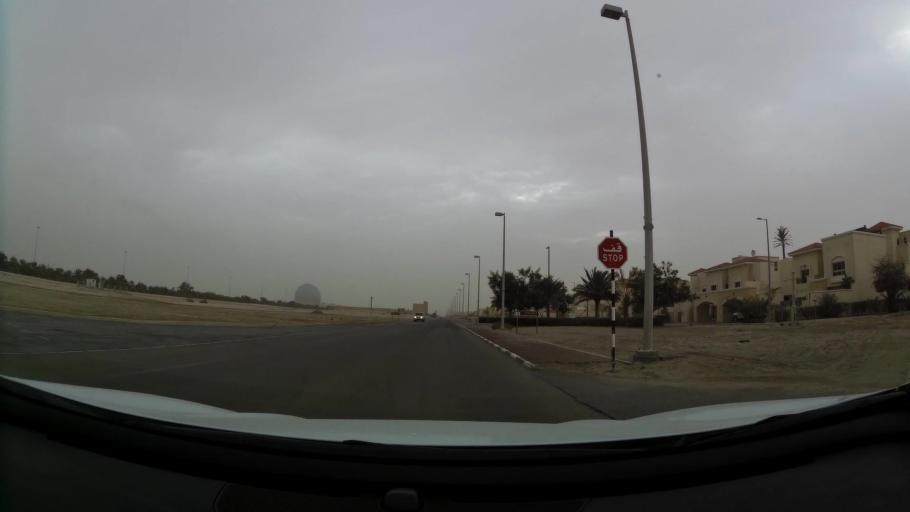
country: AE
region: Abu Dhabi
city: Abu Dhabi
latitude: 24.4312
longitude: 54.5592
